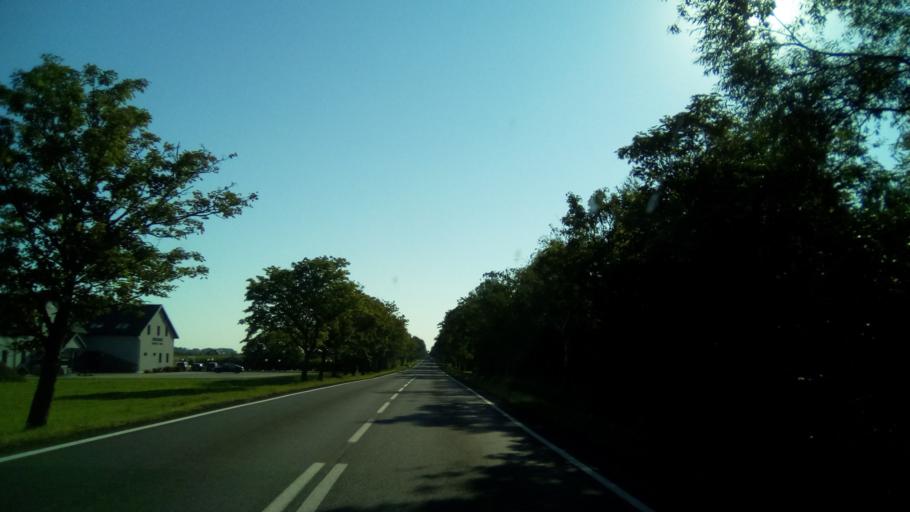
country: PL
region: Kujawsko-Pomorskie
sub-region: Powiat radziejowski
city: Radziejow
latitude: 52.6293
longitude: 18.5175
